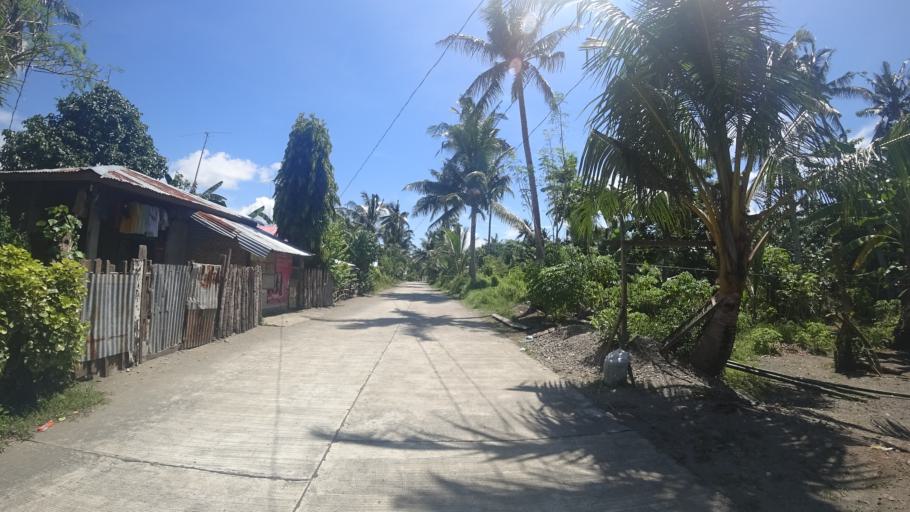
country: PH
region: Eastern Visayas
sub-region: Province of Leyte
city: Mayorga
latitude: 10.8937
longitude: 125.0116
